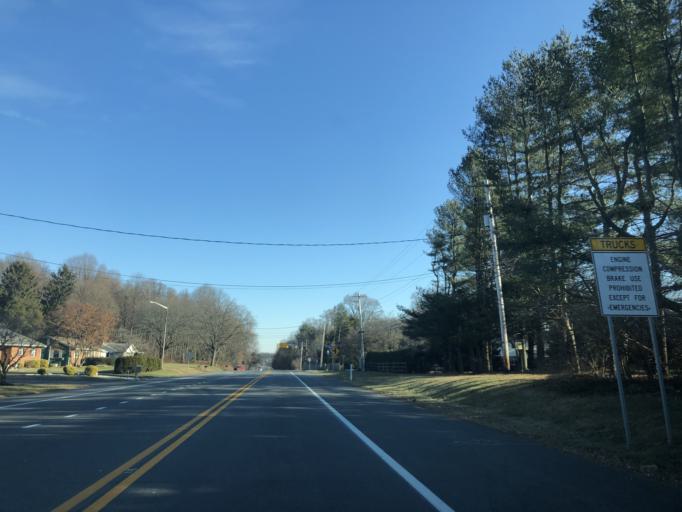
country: US
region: Delaware
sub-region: New Castle County
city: Hockessin
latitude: 39.7925
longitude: -75.7084
